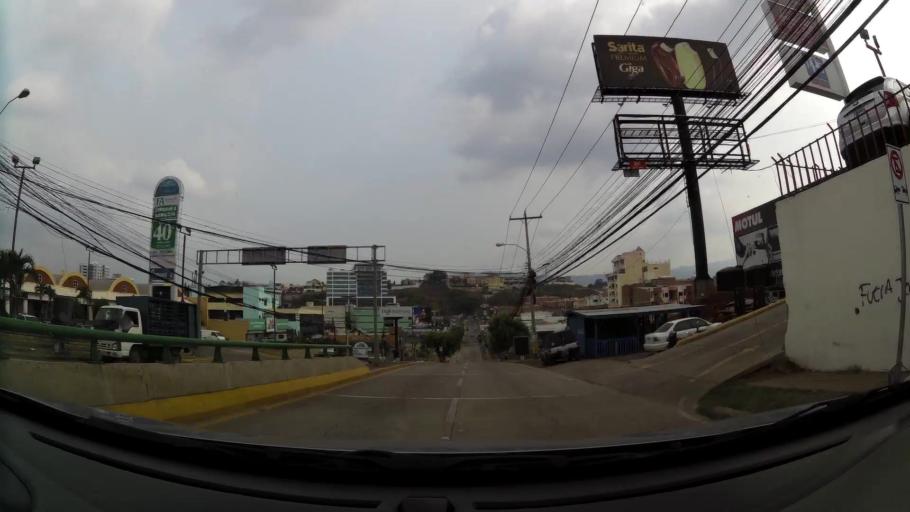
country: HN
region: Francisco Morazan
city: Tegucigalpa
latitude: 14.0857
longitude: -87.1739
